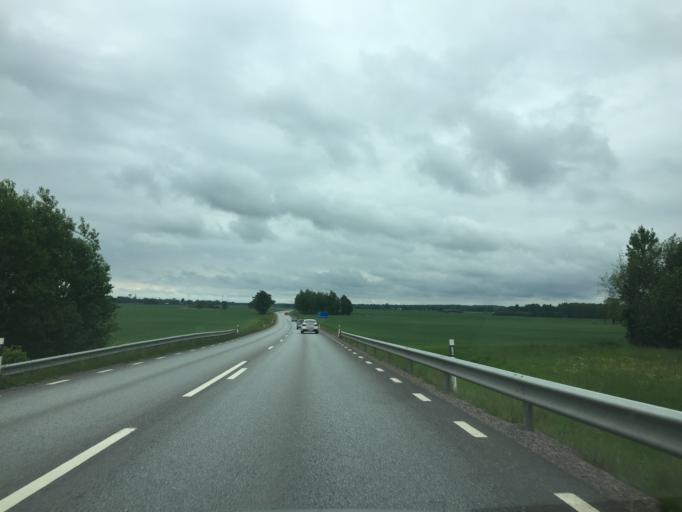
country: SE
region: OErebro
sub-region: Orebro Kommun
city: Odensbacken
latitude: 59.1541
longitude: 15.4735
